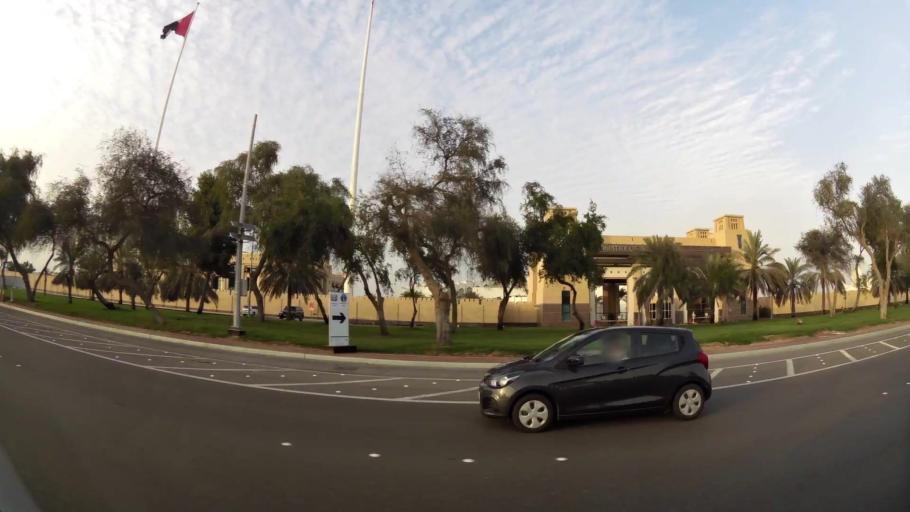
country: AE
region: Abu Dhabi
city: Abu Dhabi
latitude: 24.4095
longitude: 54.4650
